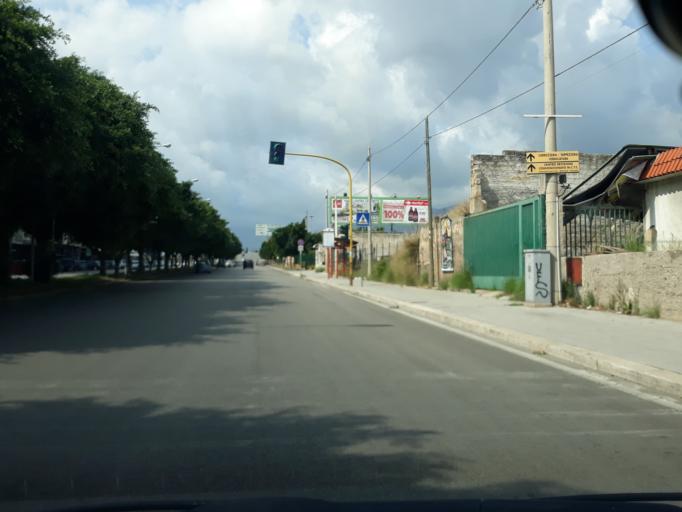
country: IT
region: Sicily
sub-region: Palermo
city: Palermo
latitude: 38.0967
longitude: 13.3442
